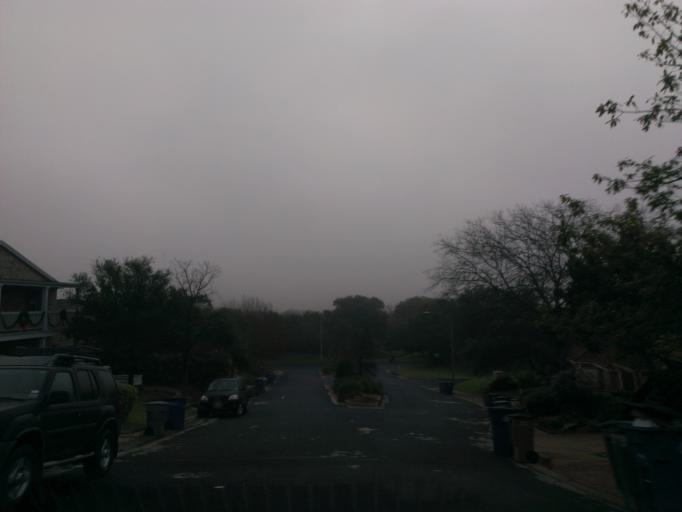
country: US
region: Texas
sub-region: Williamson County
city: Jollyville
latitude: 30.3732
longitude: -97.7909
